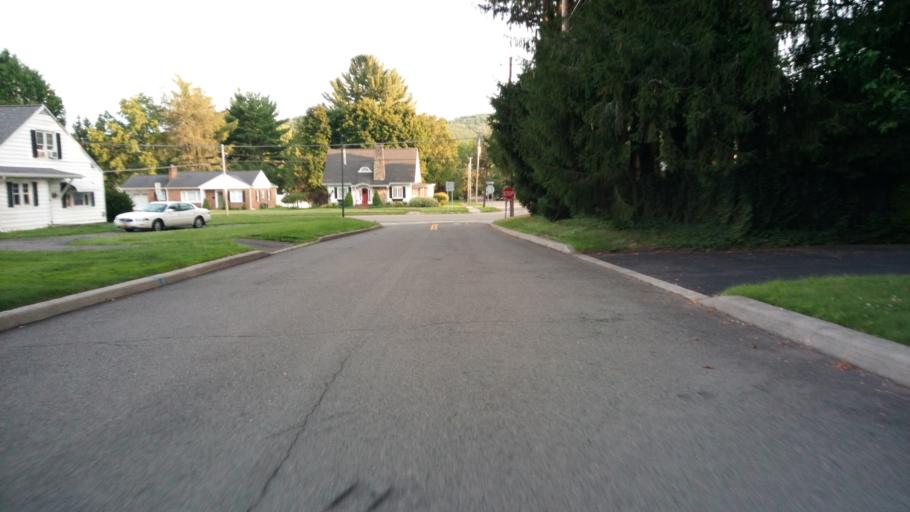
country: US
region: New York
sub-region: Chemung County
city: West Elmira
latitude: 42.0811
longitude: -76.8497
